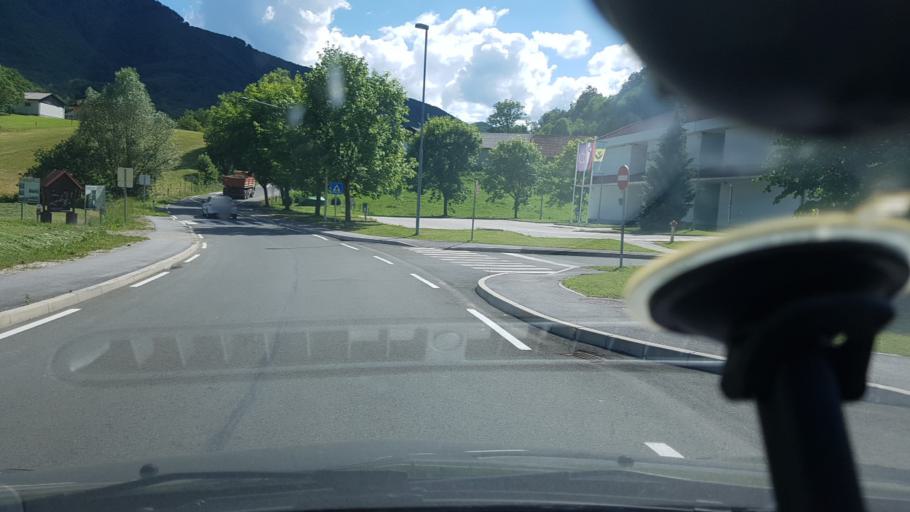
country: SI
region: Zetale
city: Zetale
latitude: 46.2736
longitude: 15.7904
